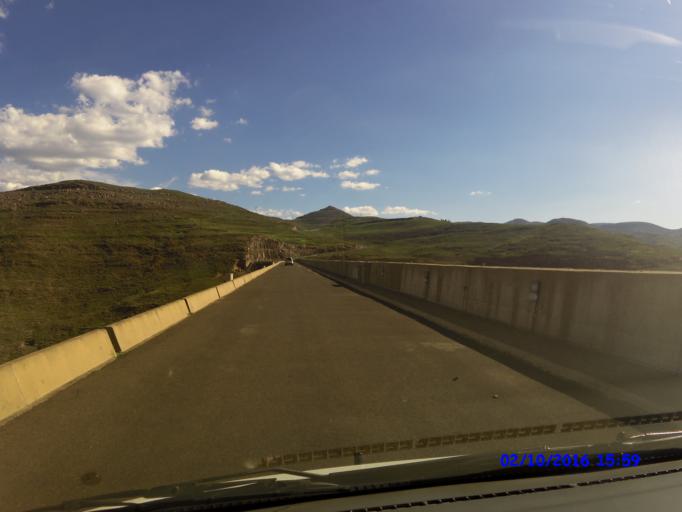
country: LS
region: Maseru
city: Nako
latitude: -29.4571
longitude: 28.0968
